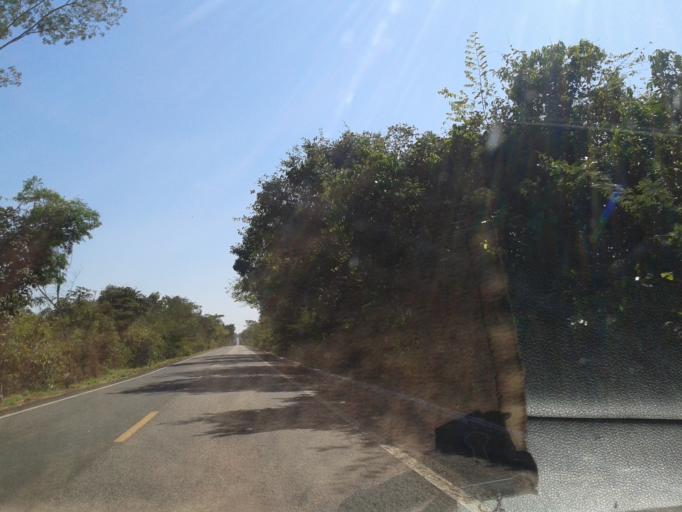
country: BR
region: Goias
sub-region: Crixas
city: Crixas
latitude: -13.9985
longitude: -50.3244
